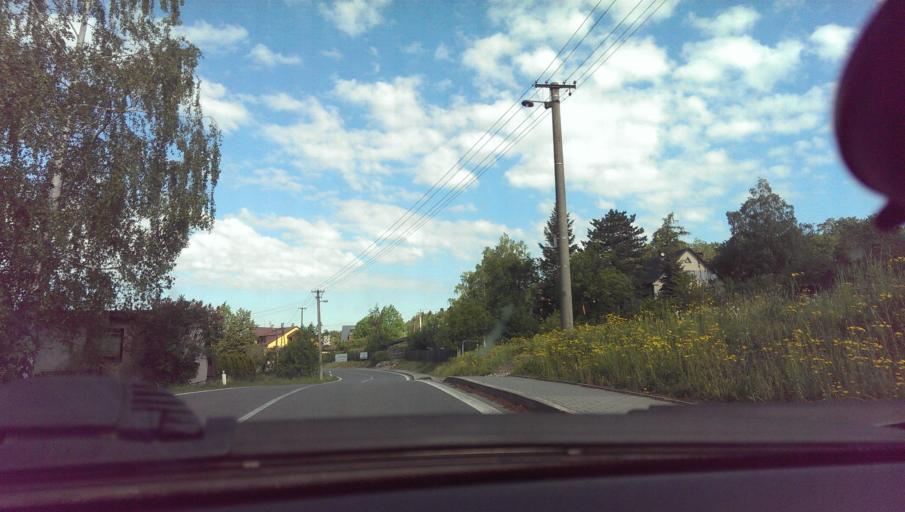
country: CZ
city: Kuncice pod Ondrejnikem
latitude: 49.5398
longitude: 18.2905
